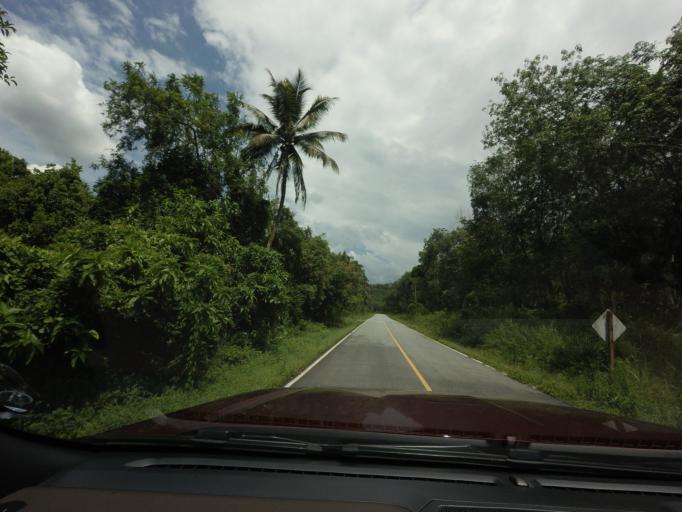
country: TH
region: Narathiwat
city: Chanae
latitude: 6.0536
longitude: 101.6877
